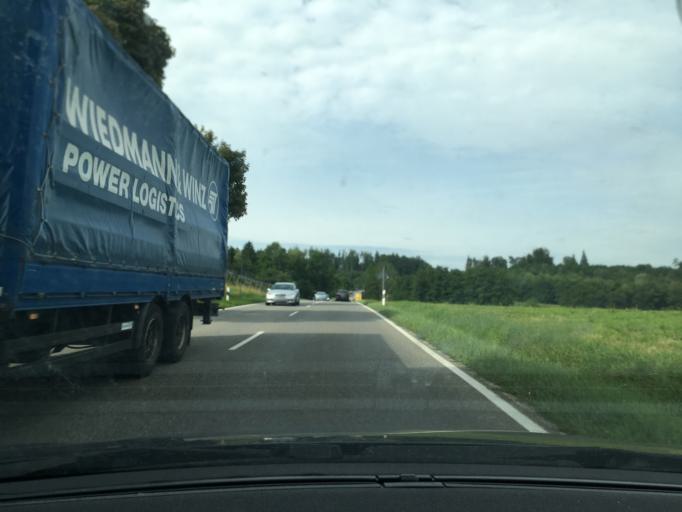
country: DE
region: Baden-Wuerttemberg
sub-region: Tuebingen Region
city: Hagnau
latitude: 47.6992
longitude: 9.3315
